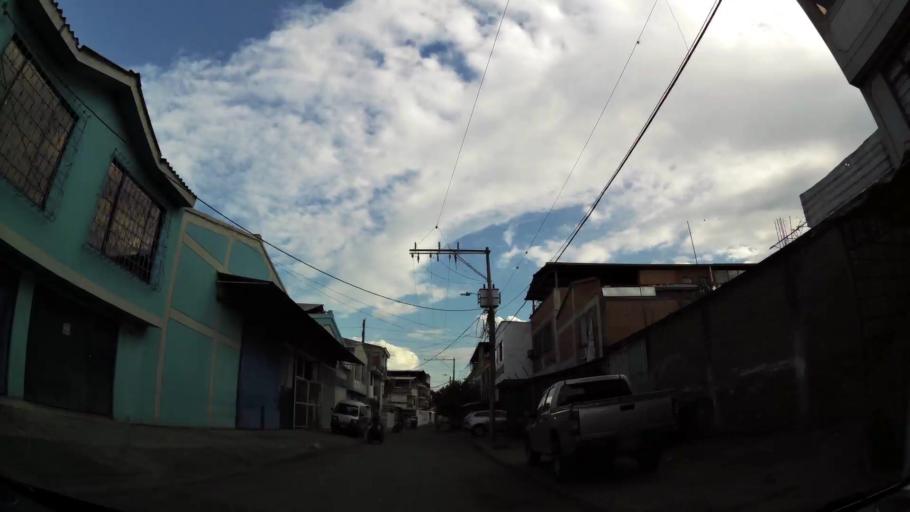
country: CO
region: Valle del Cauca
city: Cali
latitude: 3.4617
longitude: -76.5096
